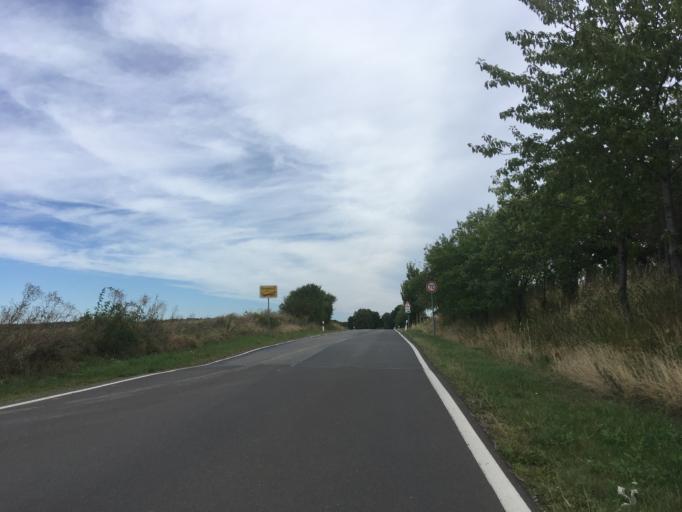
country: DE
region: Brandenburg
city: Mittenwalde
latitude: 53.2363
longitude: 13.5859
